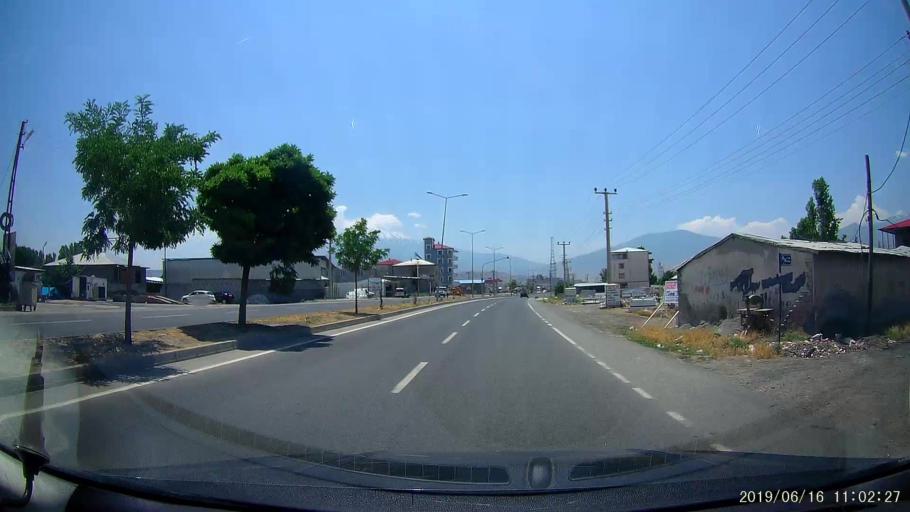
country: TR
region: Igdir
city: Igdir
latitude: 39.9068
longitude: 44.0594
